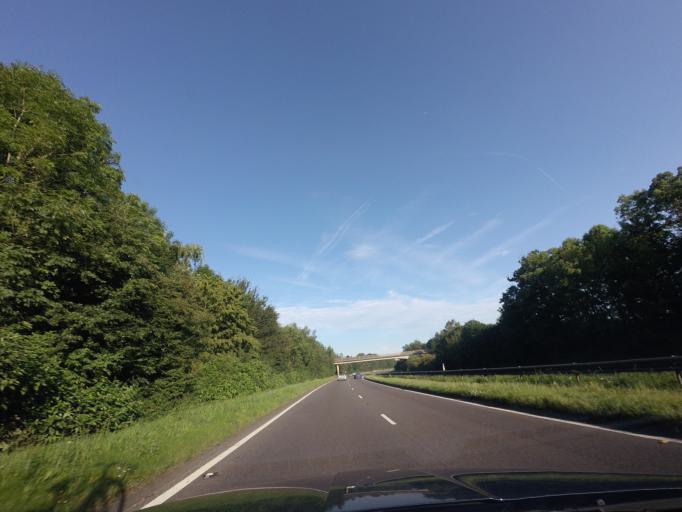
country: GB
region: England
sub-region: Derbyshire
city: Chesterfield
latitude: 53.2128
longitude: -1.3906
